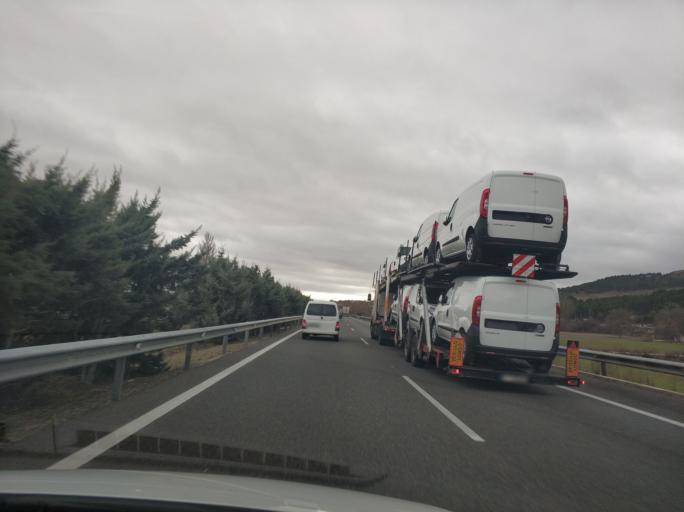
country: ES
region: Castille and Leon
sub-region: Provincia de Palencia
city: Duenas
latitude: 41.8869
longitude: -4.5320
